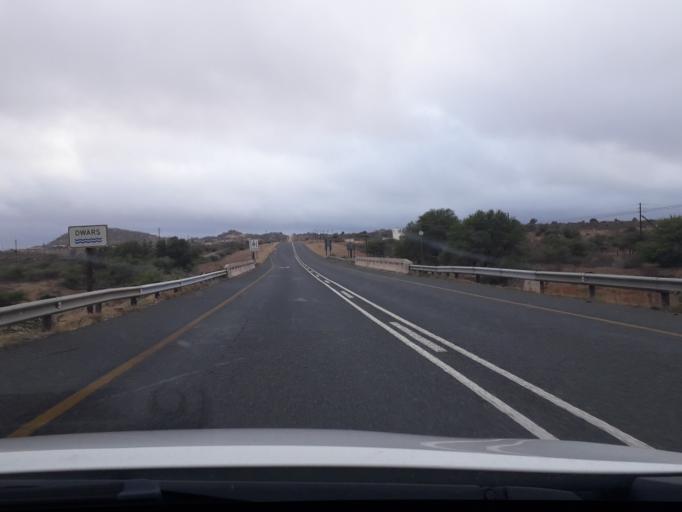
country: ZA
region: Limpopo
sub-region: Capricorn District Municipality
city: Dendron
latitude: -23.4525
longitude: 29.7392
